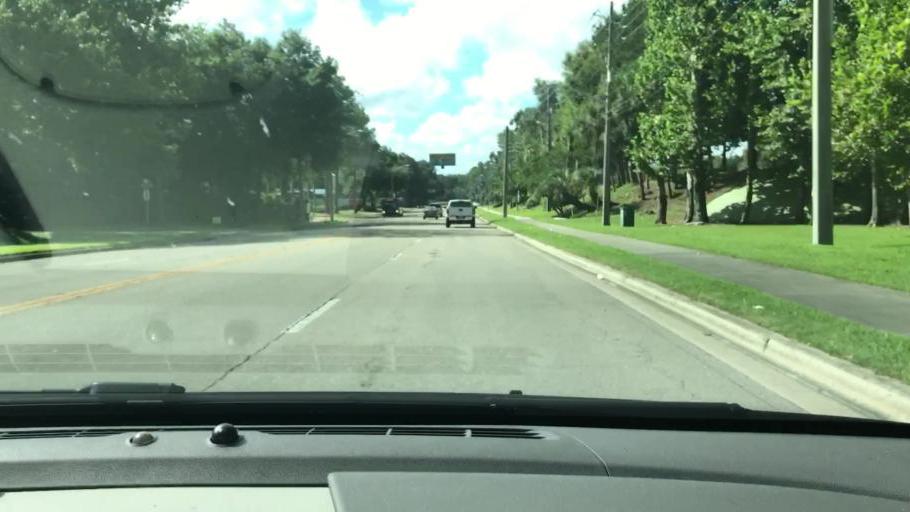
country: US
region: Florida
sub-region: Alachua County
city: Gainesville
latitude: 29.6567
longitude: -82.4089
